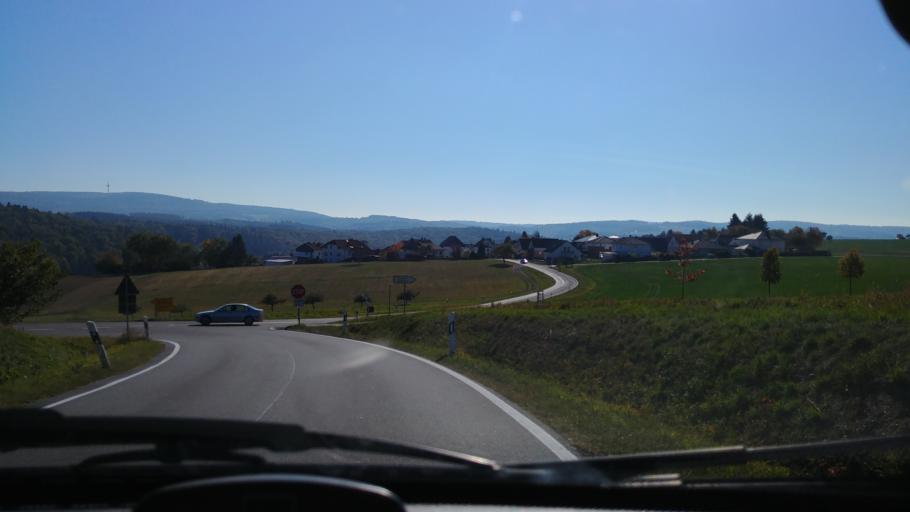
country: DE
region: Hesse
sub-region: Regierungsbezirk Darmstadt
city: Bad Schwalbach
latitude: 50.1646
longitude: 8.1044
